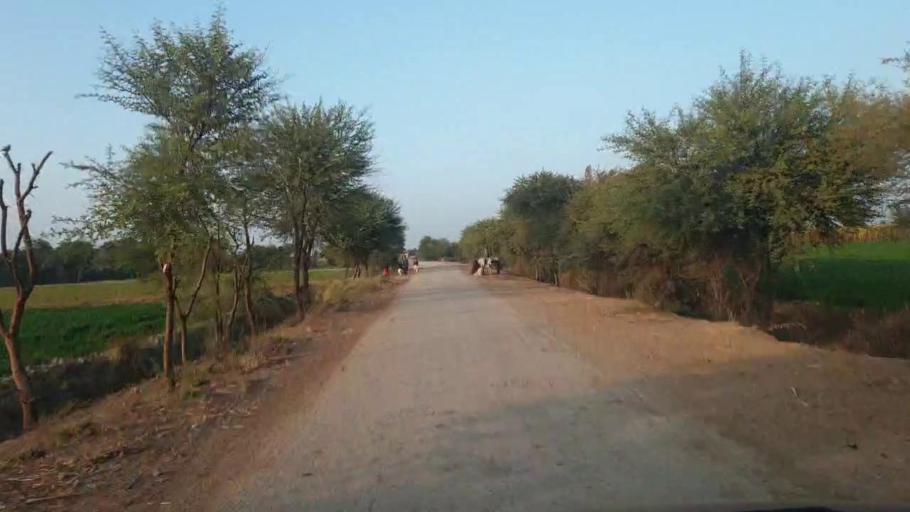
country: PK
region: Sindh
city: Berani
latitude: 25.8355
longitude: 68.7447
